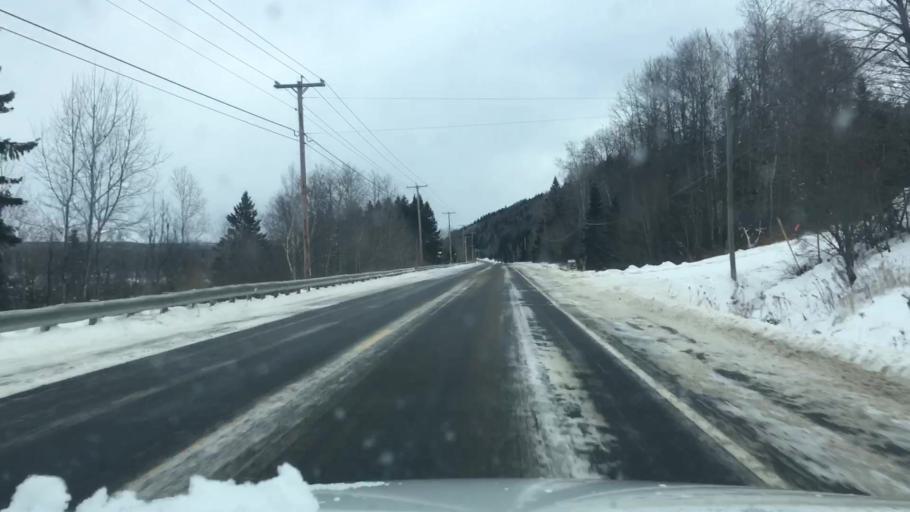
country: US
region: Maine
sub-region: Aroostook County
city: Madawaska
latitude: 47.3326
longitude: -68.2067
